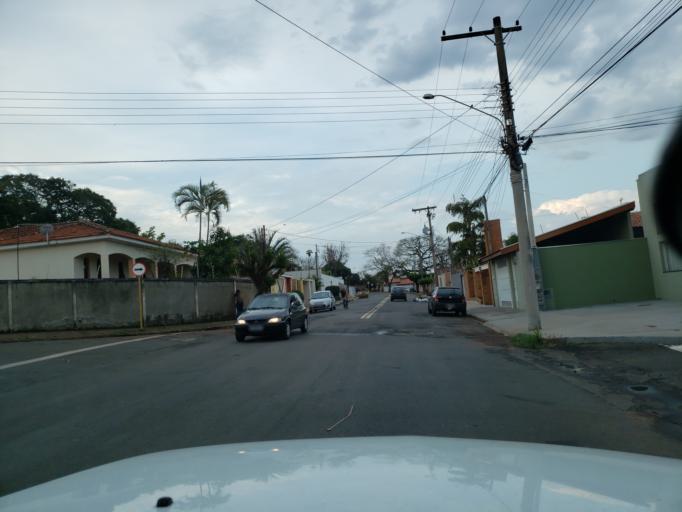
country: BR
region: Sao Paulo
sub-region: Moji-Guacu
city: Mogi-Gaucu
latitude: -22.3625
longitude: -46.9407
